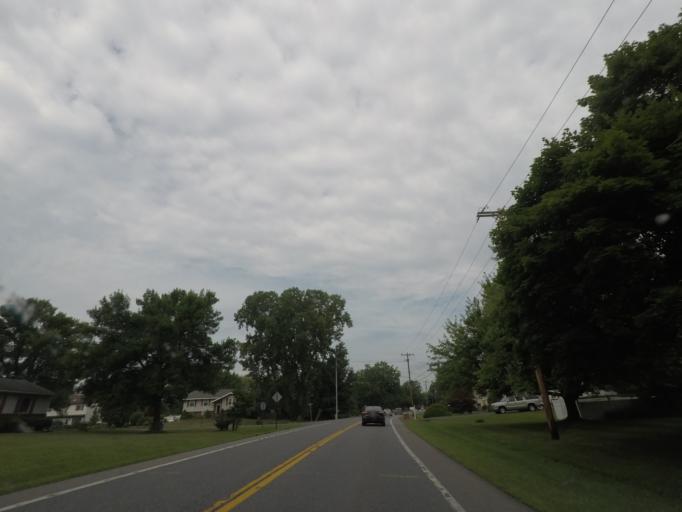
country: US
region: New York
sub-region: Saratoga County
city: Waterford
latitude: 42.8173
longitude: -73.6987
